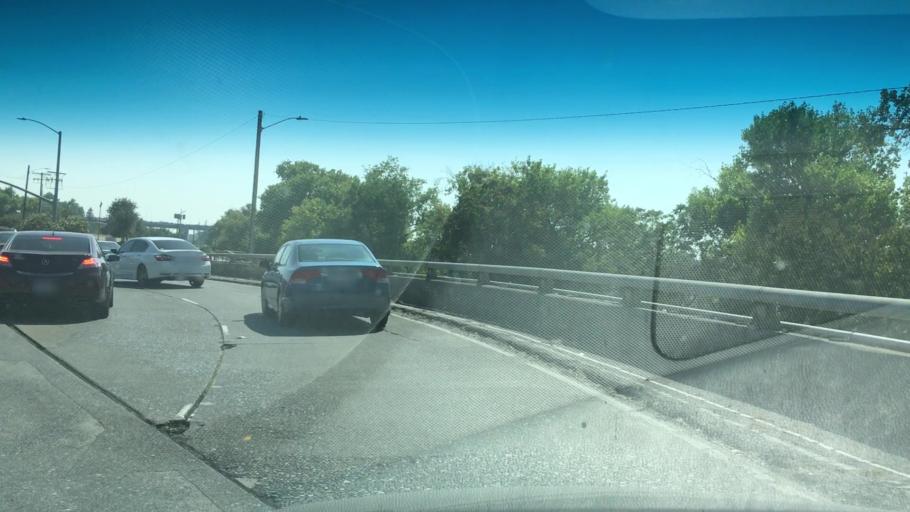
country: US
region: California
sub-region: Sacramento County
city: Sacramento
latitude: 38.5767
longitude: -121.5084
